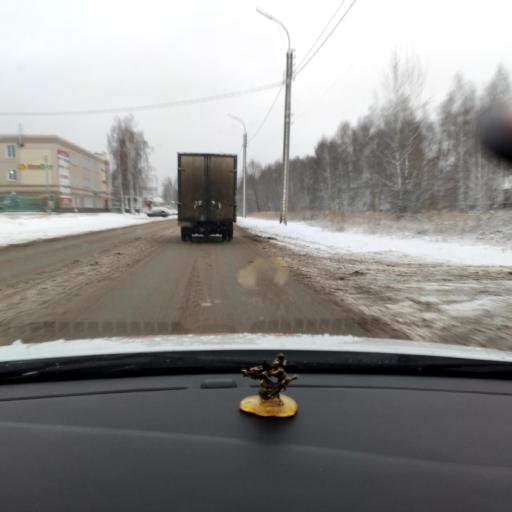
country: RU
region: Tatarstan
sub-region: Zelenodol'skiy Rayon
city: Zelenodolsk
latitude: 55.8641
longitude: 48.5485
